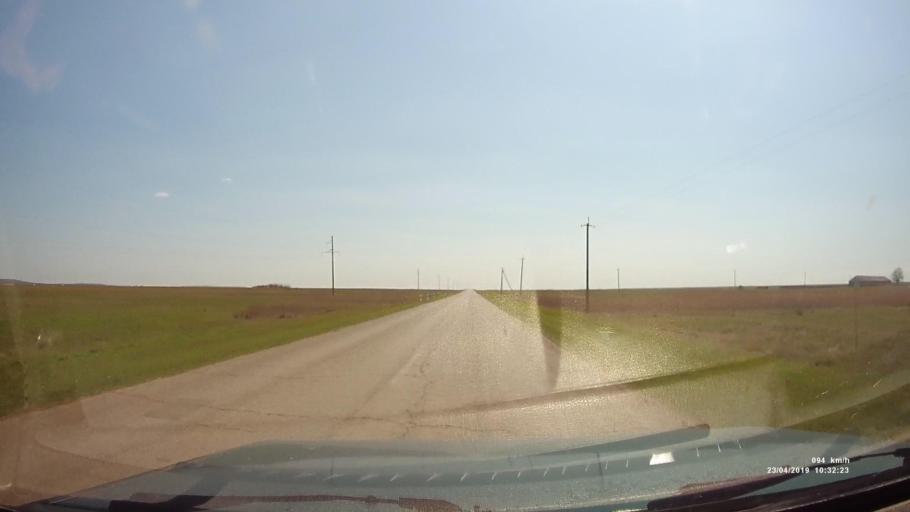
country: RU
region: Kalmykiya
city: Yashalta
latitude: 46.5805
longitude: 42.5770
